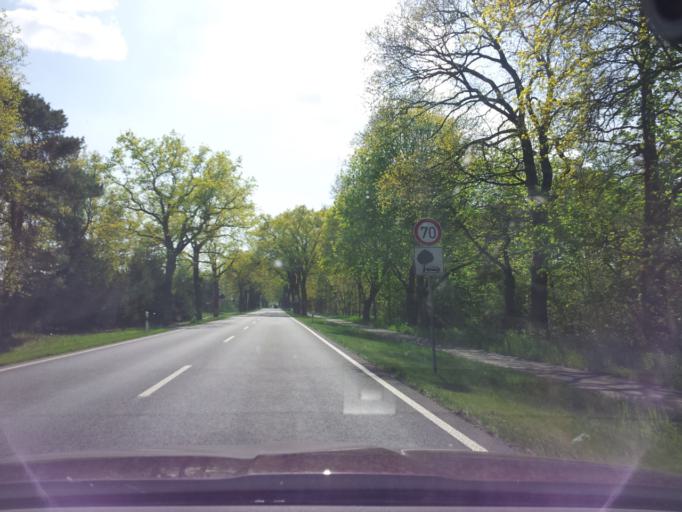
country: DE
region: Brandenburg
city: Treuenbrietzen
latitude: 52.1105
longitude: 12.8868
